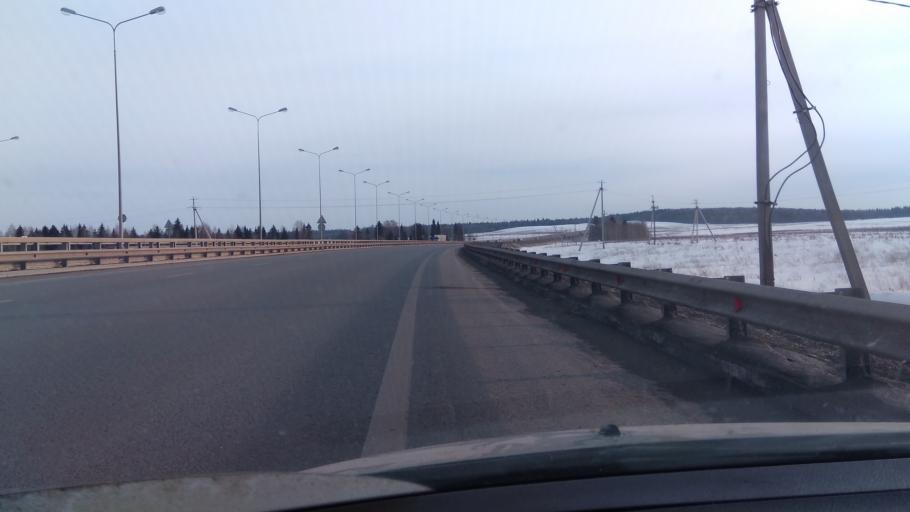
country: RU
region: Perm
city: Zvezdnyy
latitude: 57.7817
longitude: 56.3413
